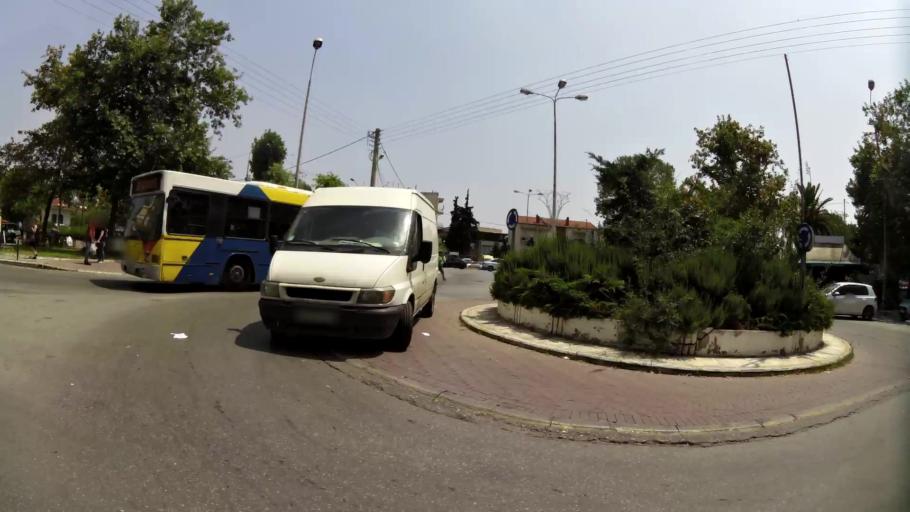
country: GR
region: Central Macedonia
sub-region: Nomos Thessalonikis
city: Evosmos
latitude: 40.6603
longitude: 22.9082
